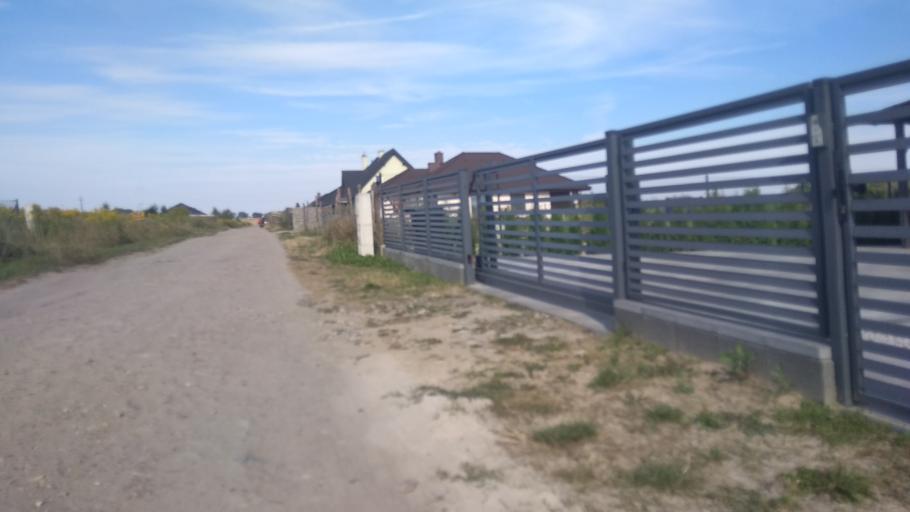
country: PL
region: Kujawsko-Pomorskie
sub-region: Powiat bydgoski
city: Osielsko
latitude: 53.2179
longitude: 18.1474
